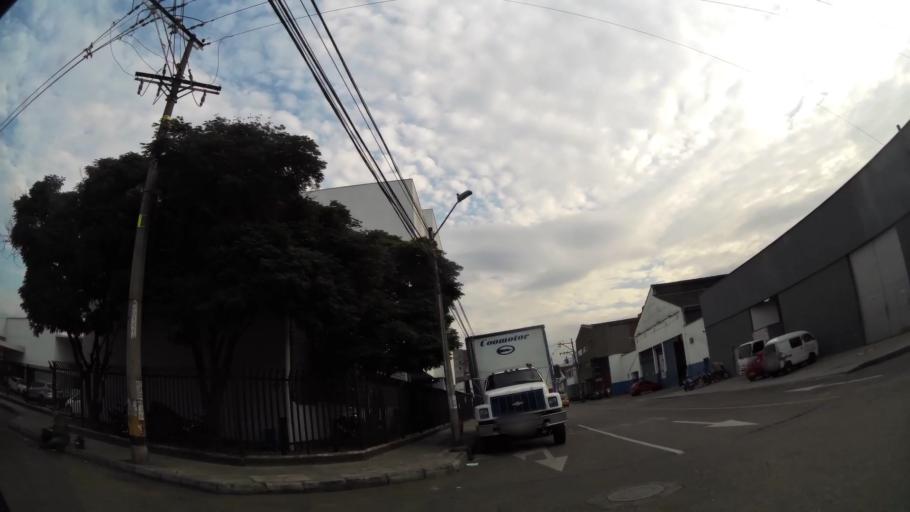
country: CO
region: Antioquia
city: Medellin
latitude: 6.2325
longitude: -75.5731
